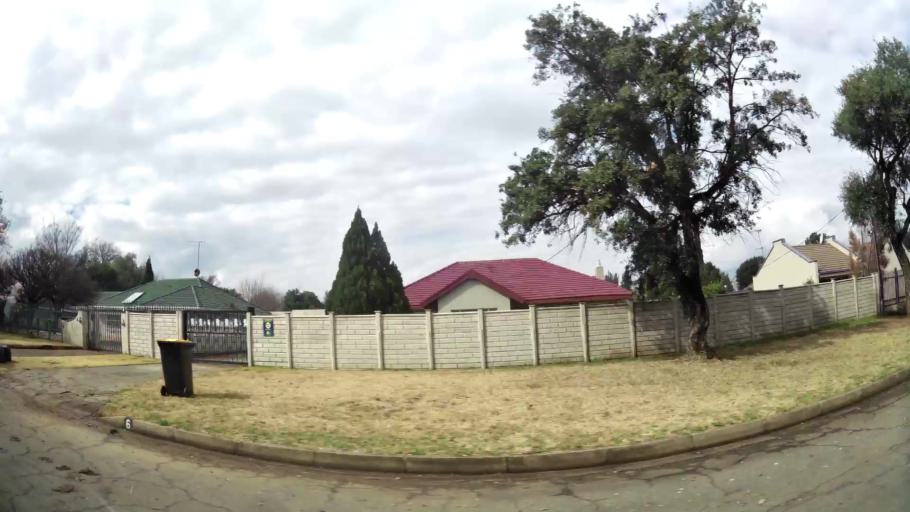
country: ZA
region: Gauteng
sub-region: Sedibeng District Municipality
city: Vereeniging
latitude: -26.6500
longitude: 27.9721
